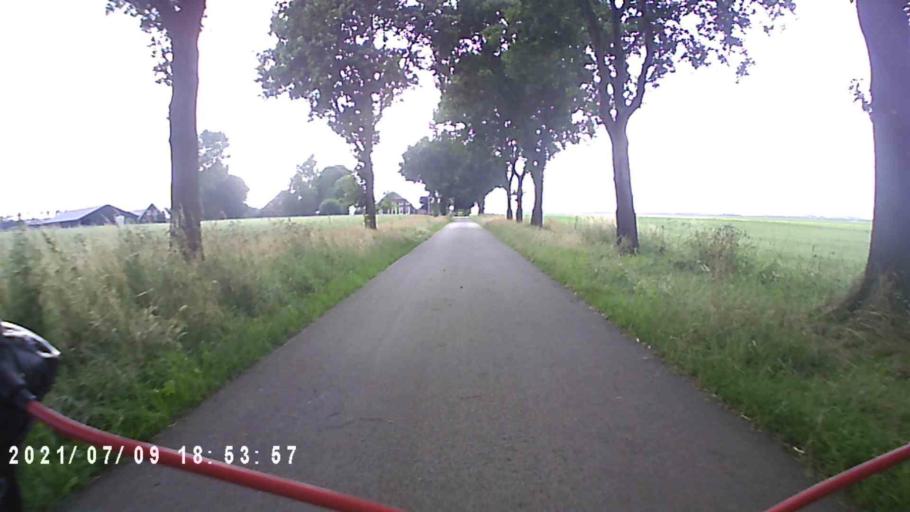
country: NL
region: Groningen
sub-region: Gemeente Stadskanaal
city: Stadskanaal
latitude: 53.0452
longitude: 6.9174
